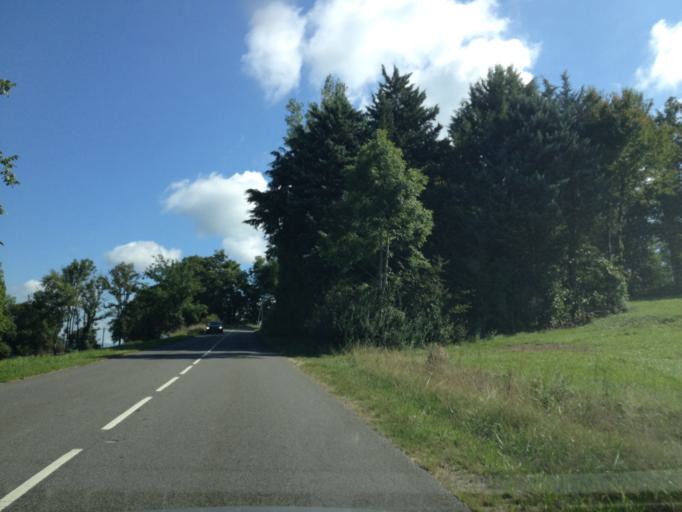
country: FR
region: Rhone-Alpes
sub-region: Departement de la Savoie
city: Gresy-sur-Aix
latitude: 45.7179
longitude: 5.9451
